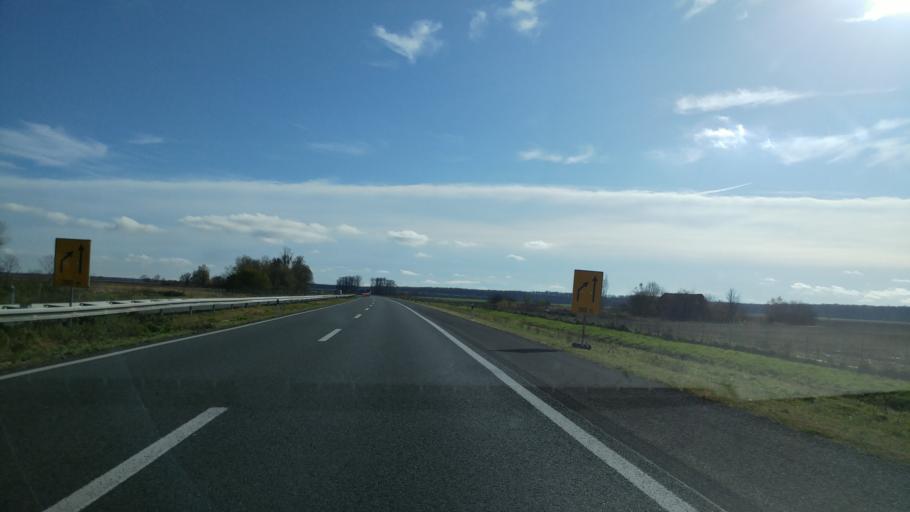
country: HR
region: Sisacko-Moslavacka
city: Lipovljani
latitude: 45.3853
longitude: 16.8700
